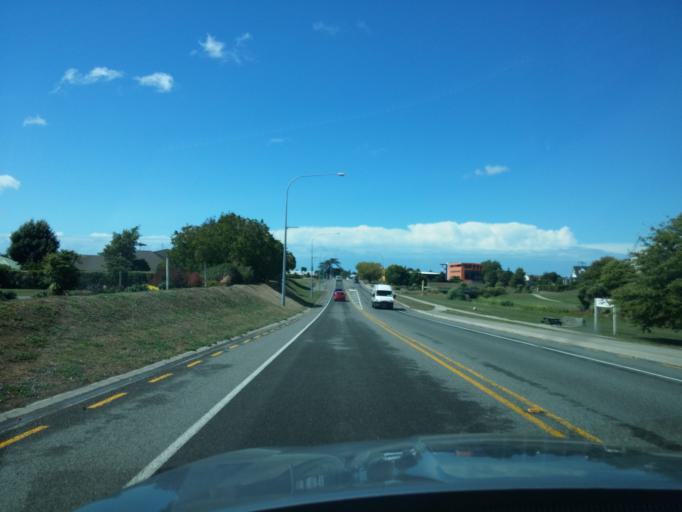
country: NZ
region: Marlborough
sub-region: Marlborough District
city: Blenheim
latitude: -41.5084
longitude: 173.9510
